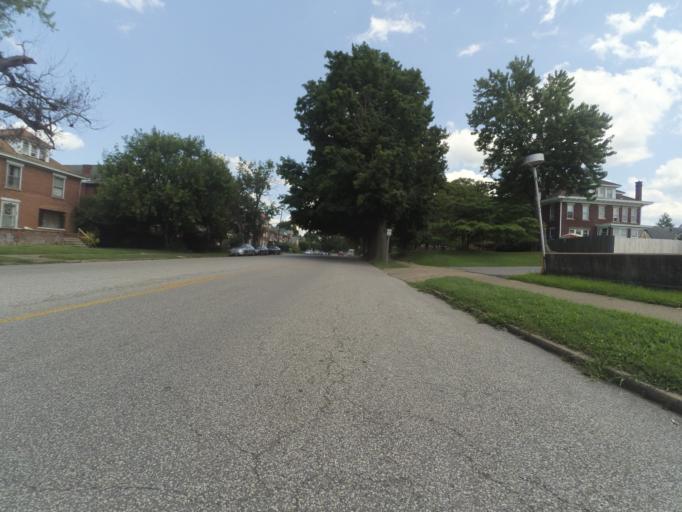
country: US
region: West Virginia
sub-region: Cabell County
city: Huntington
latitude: 38.4158
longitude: -82.4558
